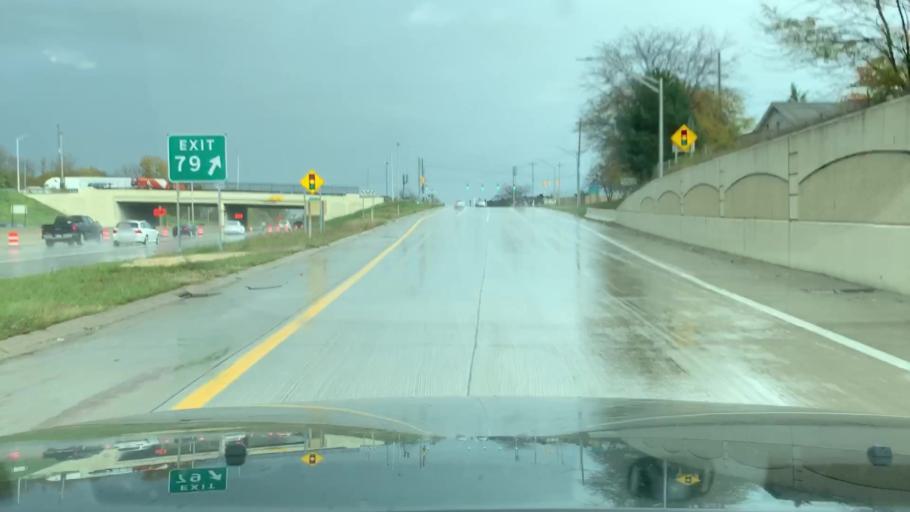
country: US
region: Michigan
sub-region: Kent County
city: Grand Rapids
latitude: 42.9732
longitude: -85.6417
